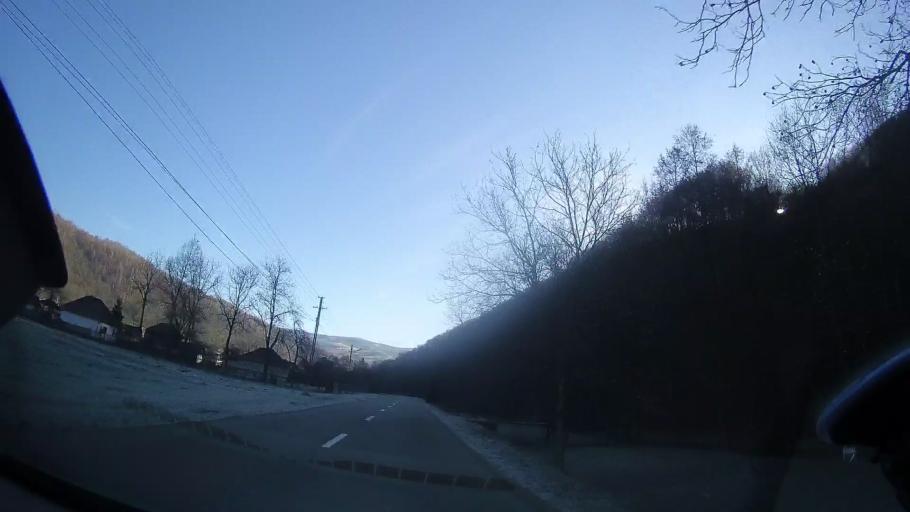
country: RO
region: Bihor
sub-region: Comuna Bulz
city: Bulz
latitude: 46.9077
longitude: 22.6806
